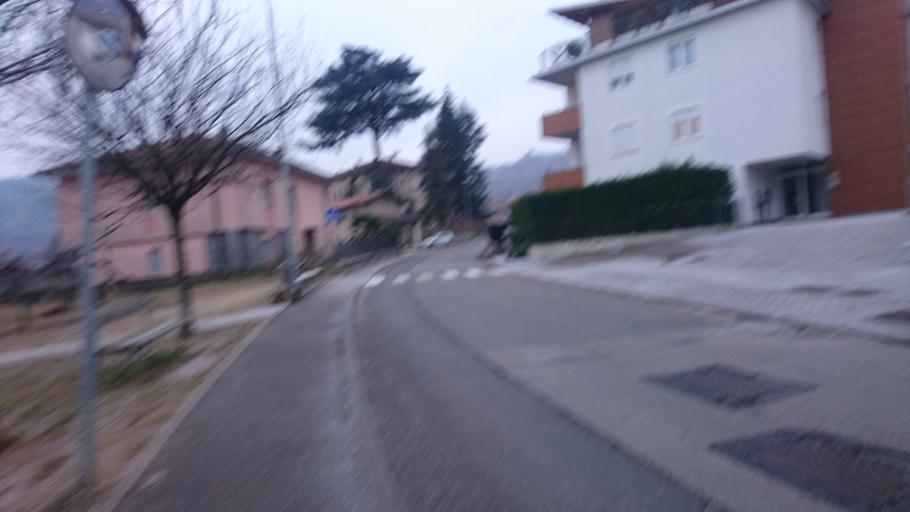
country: IT
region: Trentino-Alto Adige
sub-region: Provincia di Trento
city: Mori
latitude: 45.8490
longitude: 10.9785
